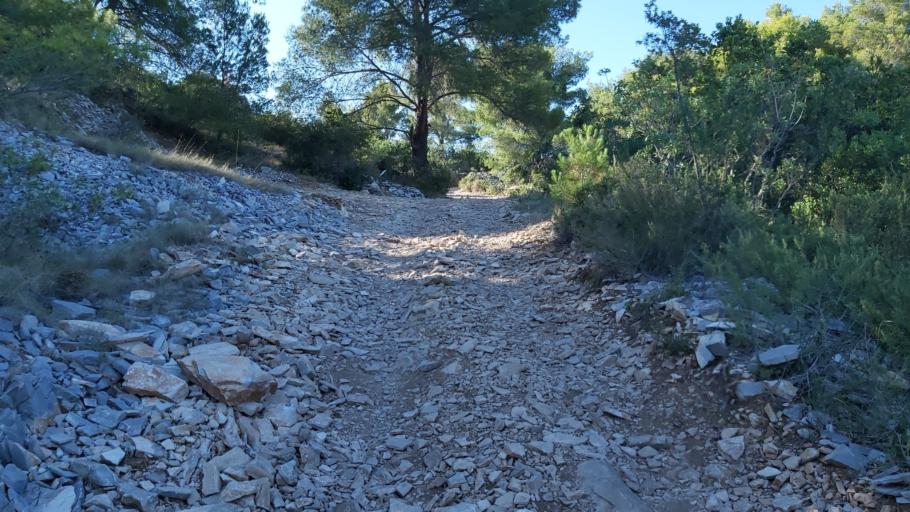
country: HR
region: Splitsko-Dalmatinska
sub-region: Grad Trogir
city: Trogir
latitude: 43.3733
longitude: 16.2870
